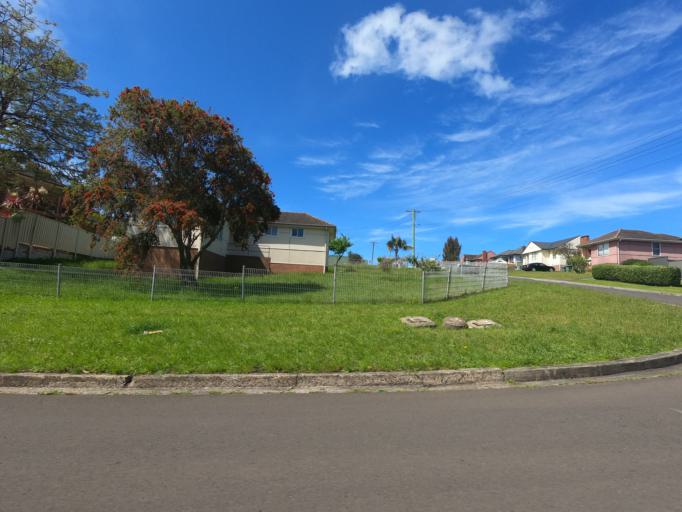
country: AU
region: New South Wales
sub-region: Wollongong
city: Lake Heights
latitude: -34.4898
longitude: 150.8777
